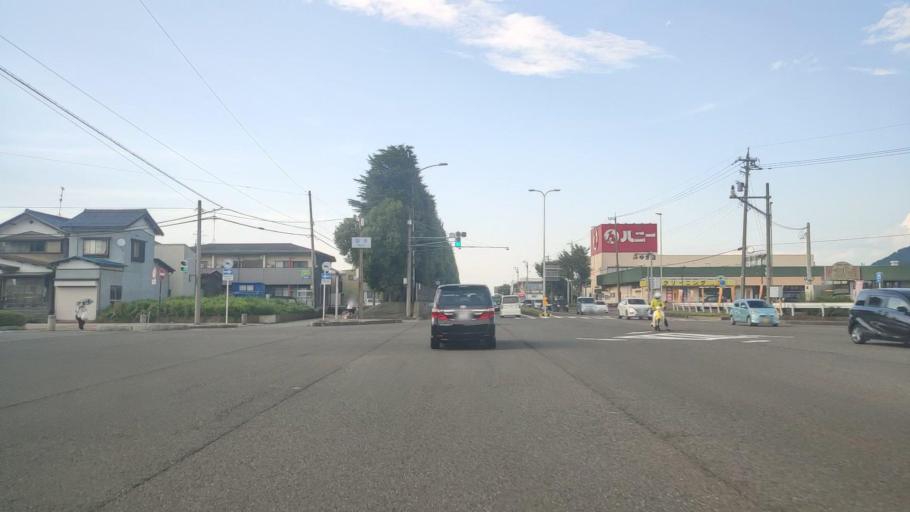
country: JP
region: Fukui
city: Sabae
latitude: 35.9749
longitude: 136.1933
